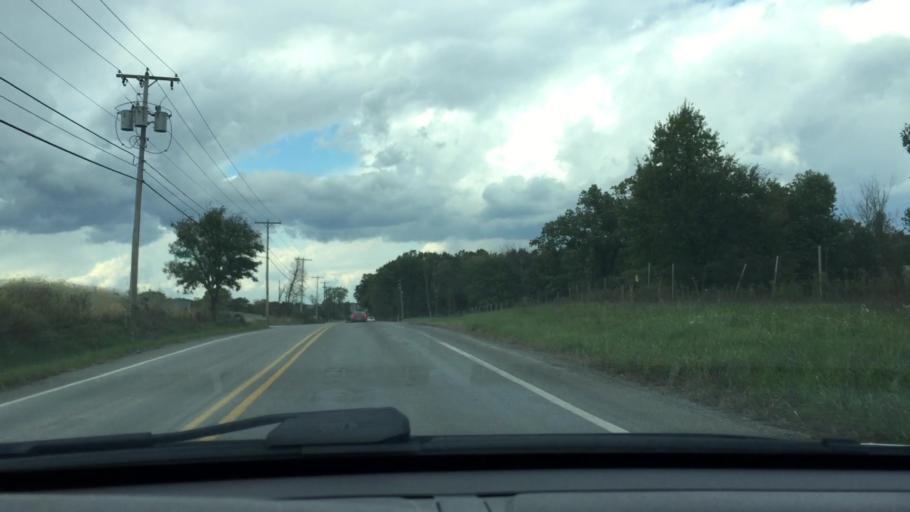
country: US
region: Pennsylvania
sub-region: Lawrence County
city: Bessemer
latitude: 40.9907
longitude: -80.4369
